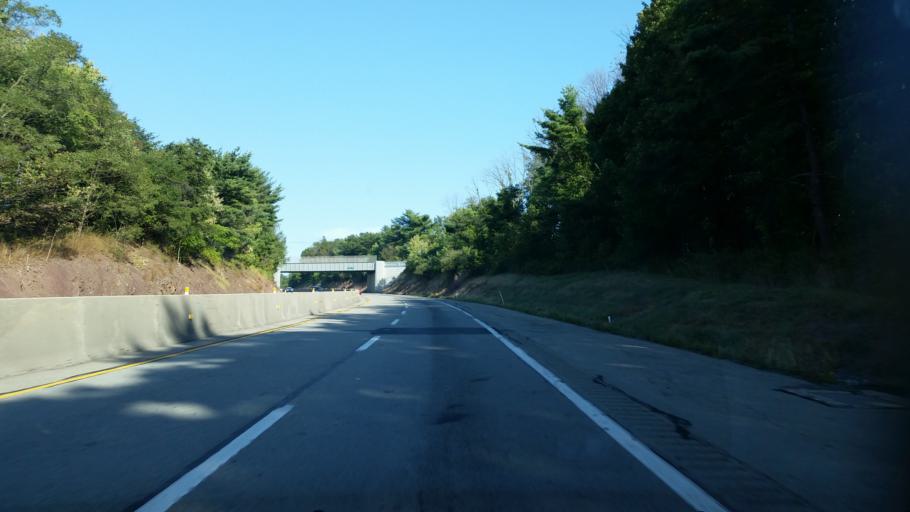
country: US
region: Pennsylvania
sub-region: Fulton County
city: McConnellsburg
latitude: 40.0437
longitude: -78.0412
